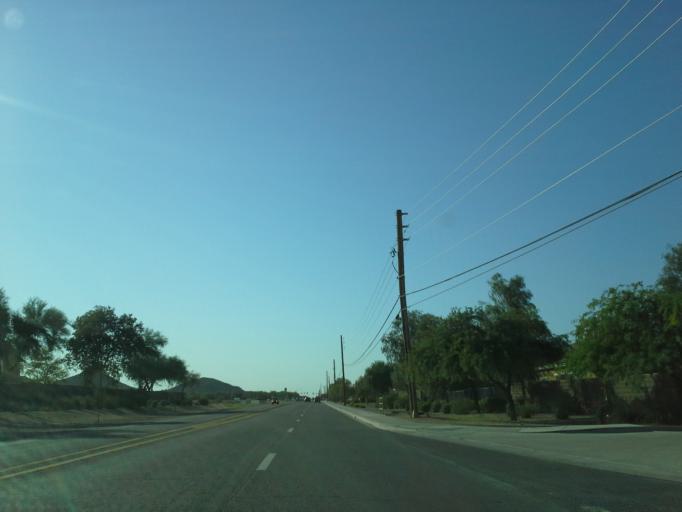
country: US
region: Arizona
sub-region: Pinal County
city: San Tan Valley
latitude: 33.1559
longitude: -111.5583
